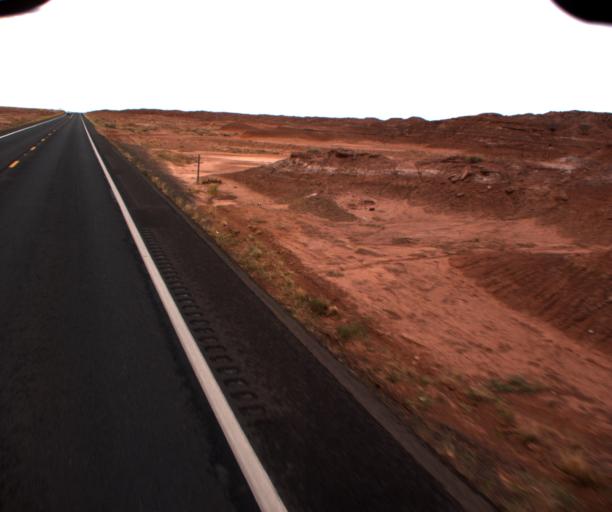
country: US
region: Arizona
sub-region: Coconino County
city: Tuba City
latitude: 36.1037
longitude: -111.2810
